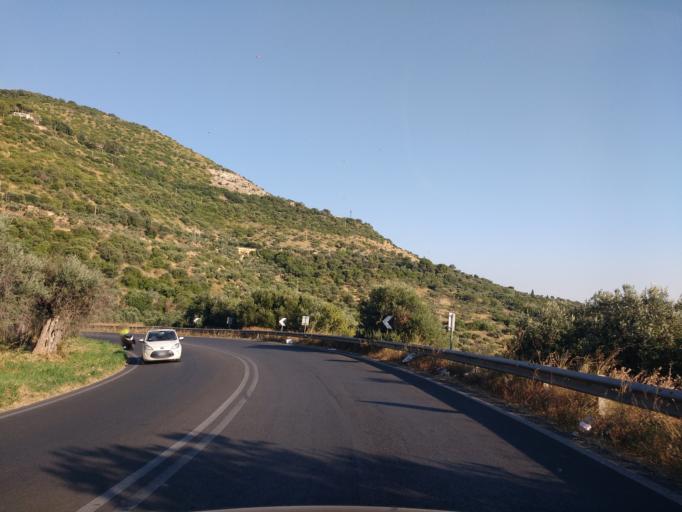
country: IT
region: Latium
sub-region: Citta metropolitana di Roma Capitale
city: Tivoli
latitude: 41.9492
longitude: 12.7914
